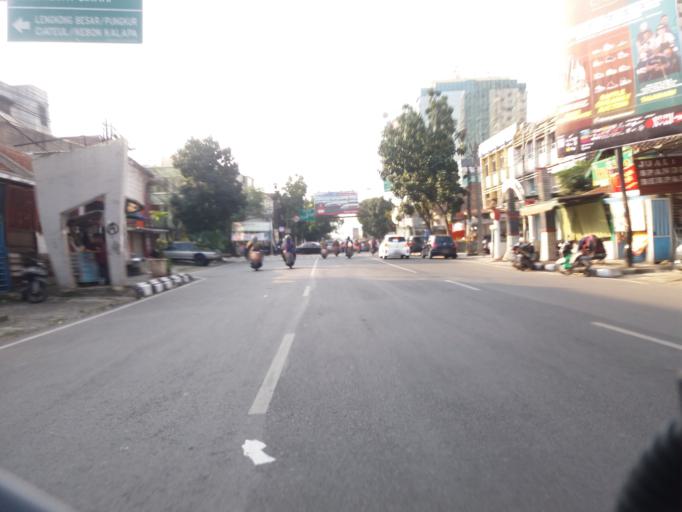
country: ID
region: West Java
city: Bandung
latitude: -6.9244
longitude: 107.6174
